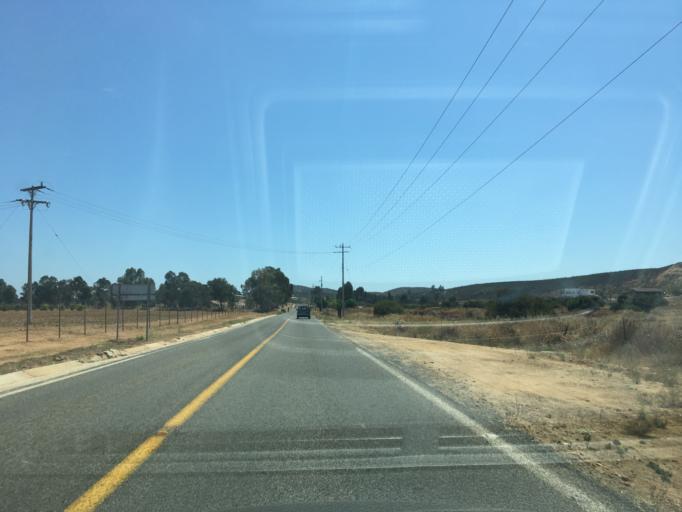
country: MX
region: Baja California
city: El Sauzal
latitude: 32.0039
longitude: -116.6818
